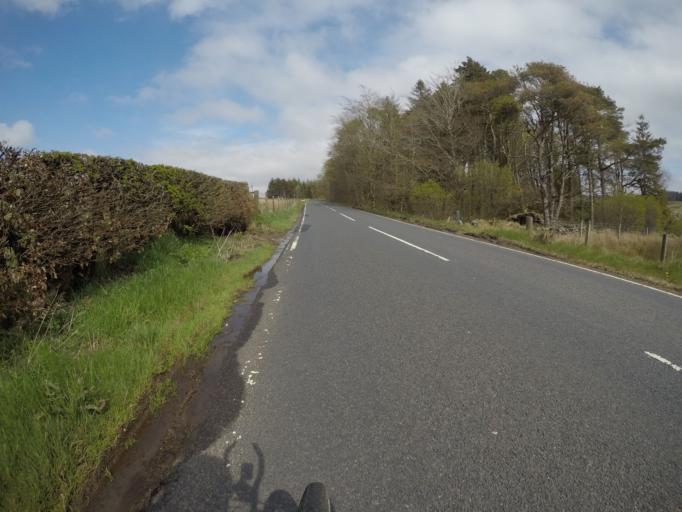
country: GB
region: Scotland
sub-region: East Renfrewshire
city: Neilston
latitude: 55.7186
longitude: -4.4345
